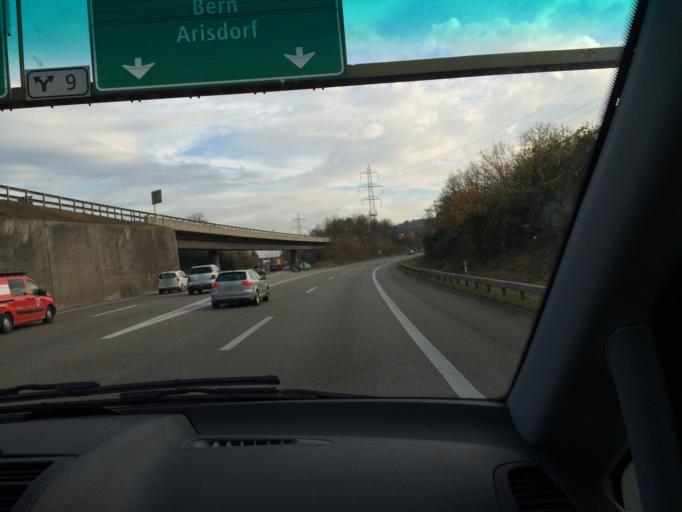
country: CH
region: Aargau
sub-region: Bezirk Rheinfelden
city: Kaiseraugst
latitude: 47.5296
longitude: 7.7280
